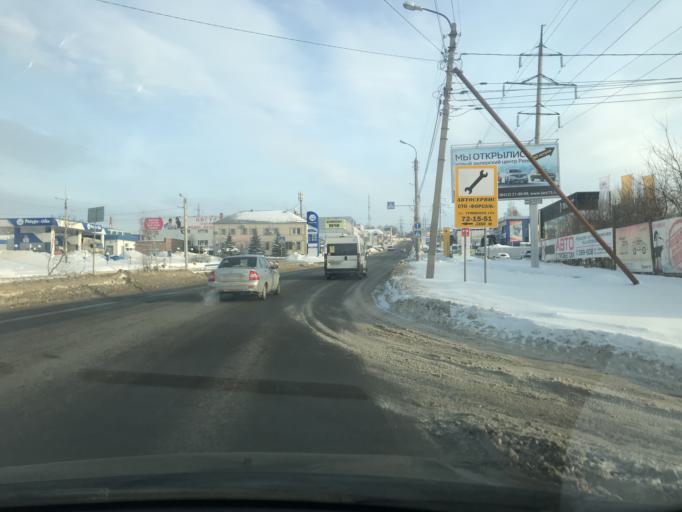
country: RU
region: Ulyanovsk
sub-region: Ulyanovskiy Rayon
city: Ulyanovsk
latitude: 54.3278
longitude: 48.3577
